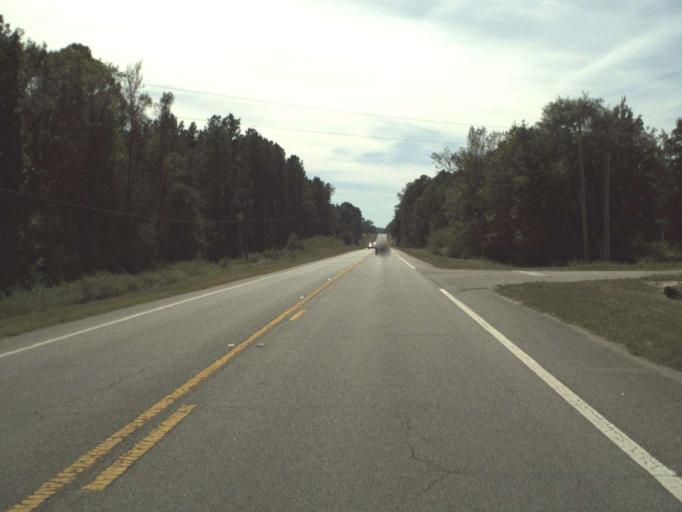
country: US
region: Florida
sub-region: Washington County
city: Chipley
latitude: 30.6693
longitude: -85.5747
